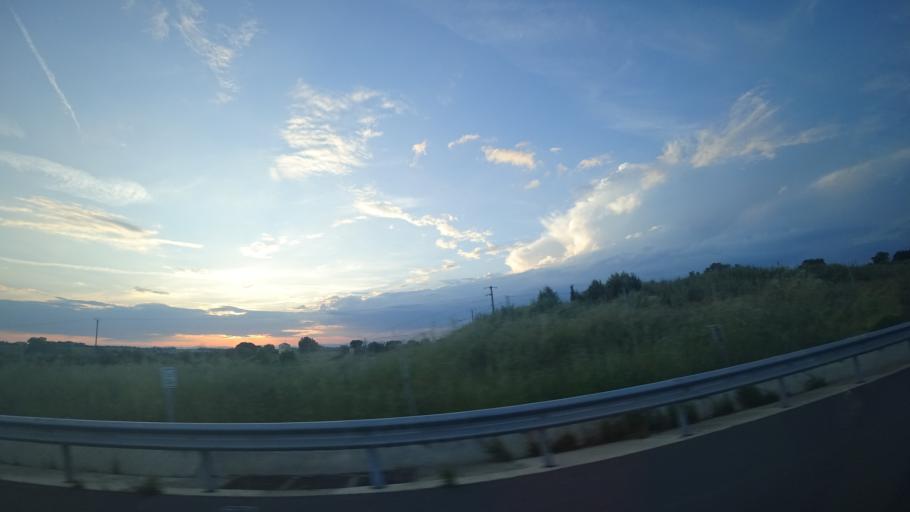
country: FR
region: Languedoc-Roussillon
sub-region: Departement de l'Herault
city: Servian
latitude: 43.3838
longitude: 3.3097
